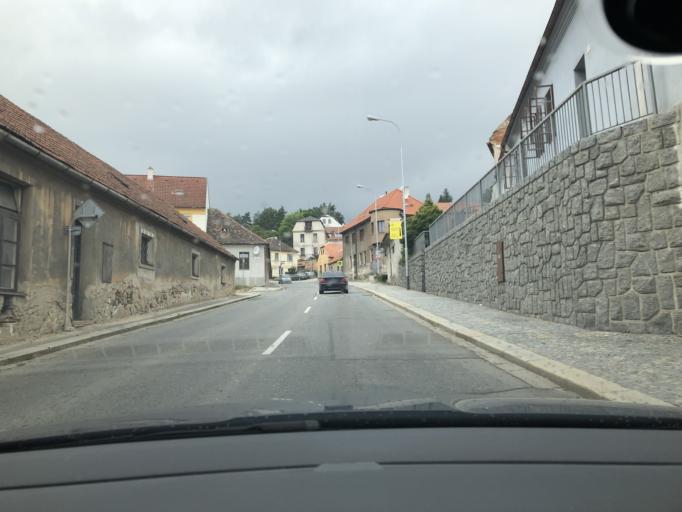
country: CZ
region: Vysocina
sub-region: Okres Trebic
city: Trebic
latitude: 49.2171
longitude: 15.8756
